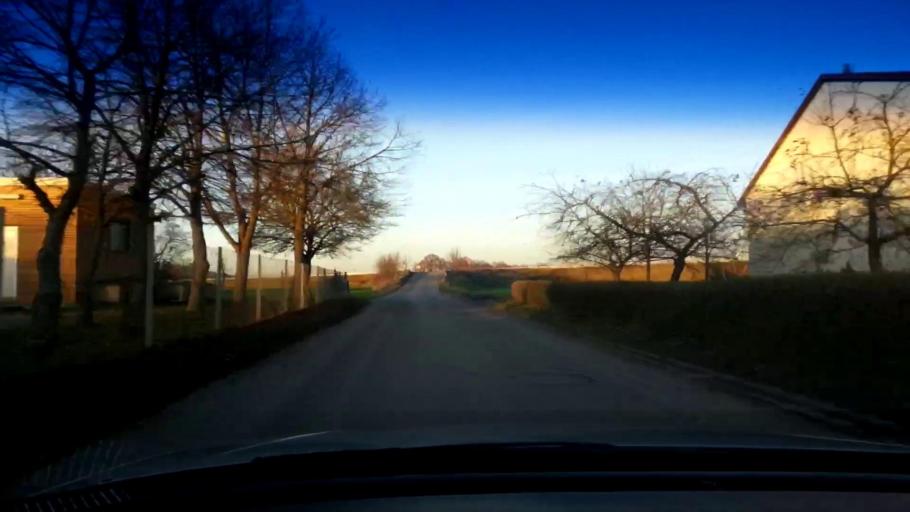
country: DE
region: Bavaria
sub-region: Upper Franconia
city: Ebensfeld
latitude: 50.0595
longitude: 10.9487
